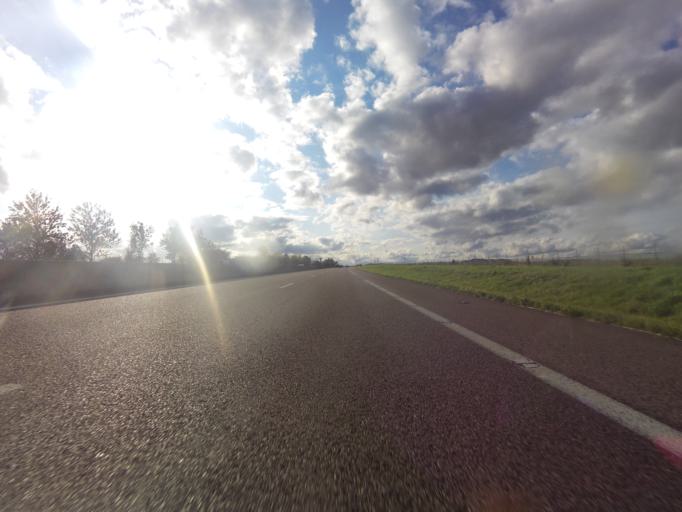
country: FR
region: Picardie
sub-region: Departement de la Somme
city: Hornoy-le-Bourg
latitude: 49.8124
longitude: 1.8724
